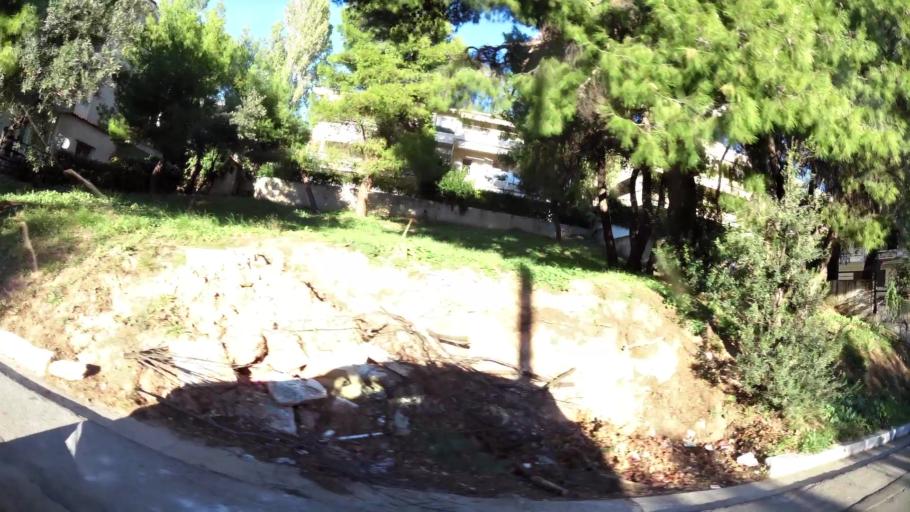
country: GR
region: Attica
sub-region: Nomarchia Athinas
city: Nea Erythraia
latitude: 38.0861
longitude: 23.8296
